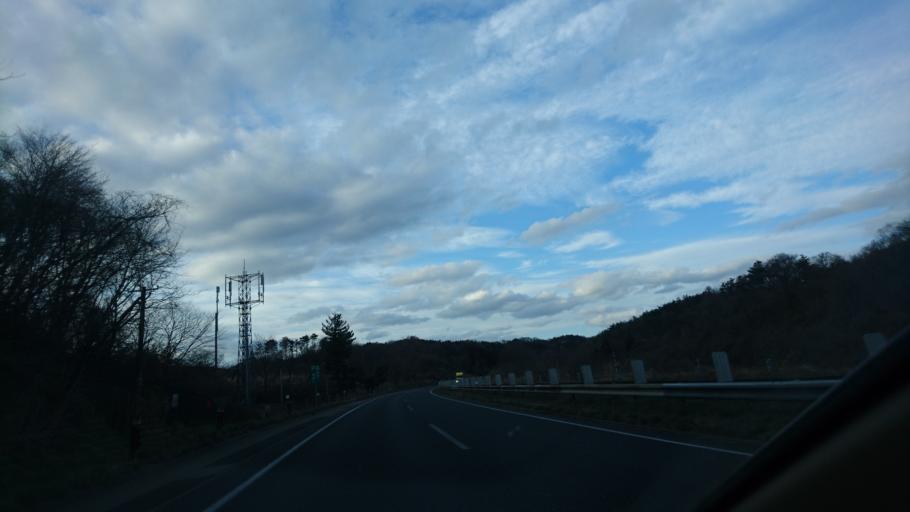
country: JP
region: Iwate
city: Ichinoseki
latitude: 38.8224
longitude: 141.0946
